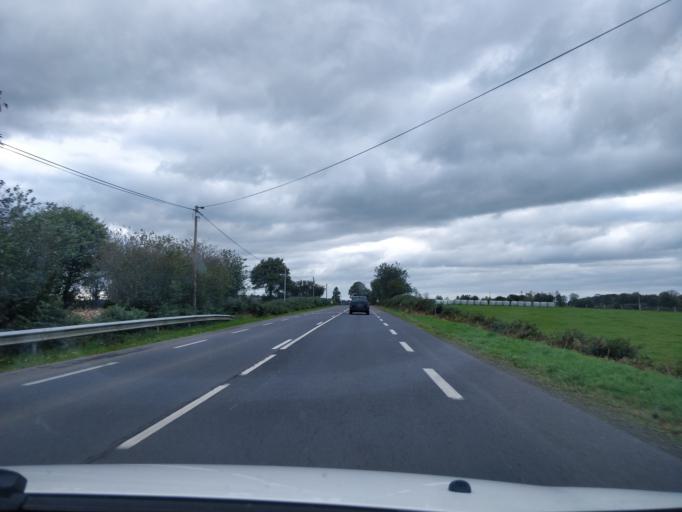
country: FR
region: Lower Normandy
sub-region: Departement du Calvados
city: Saint-Sever-Calvados
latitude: 48.8216
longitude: -1.1187
